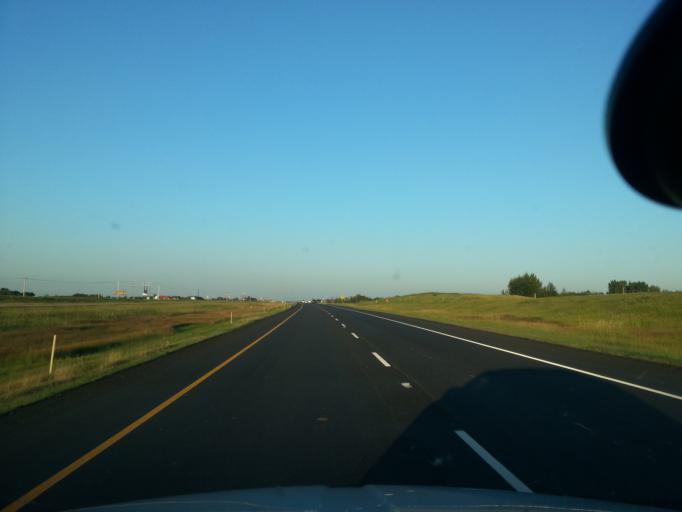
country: CA
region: Alberta
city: Spruce Grove
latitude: 53.5695
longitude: -113.8845
